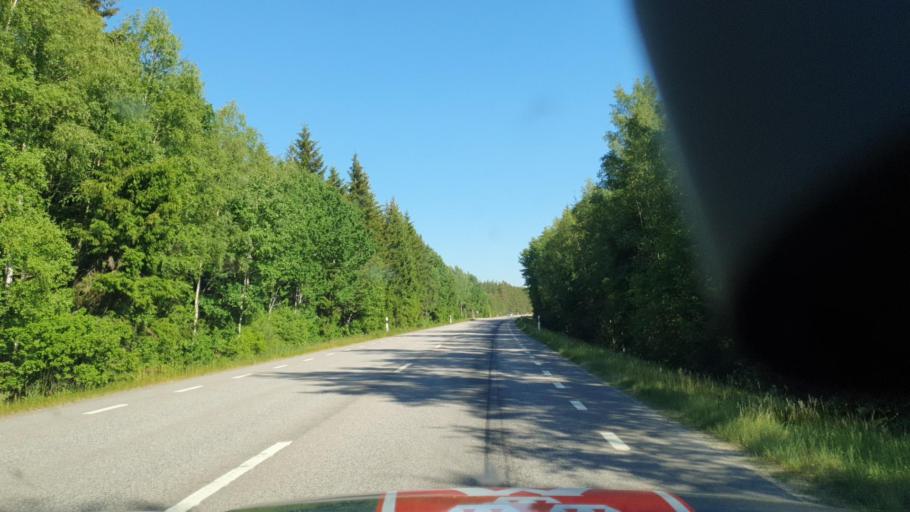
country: SE
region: Kalmar
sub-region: Emmaboda Kommun
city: Emmaboda
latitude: 56.8954
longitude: 15.6119
